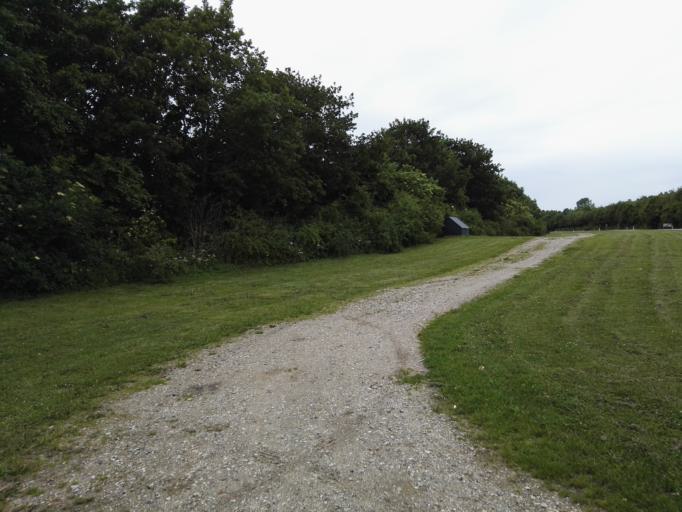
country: DK
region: Zealand
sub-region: Roskilde Kommune
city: Jyllinge
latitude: 55.7734
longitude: 12.1302
